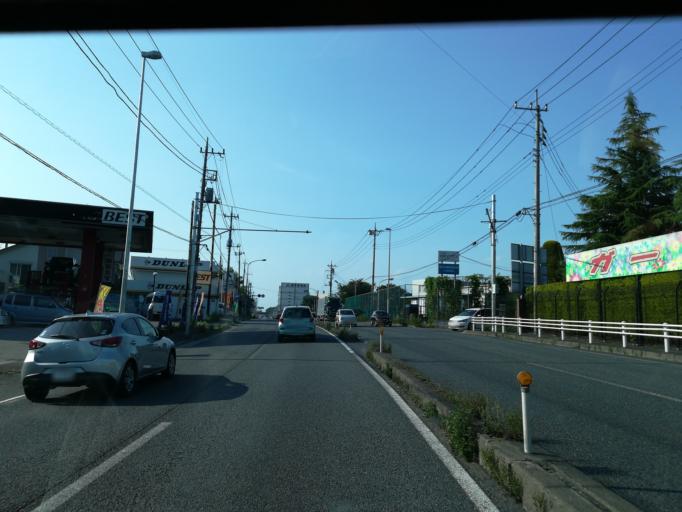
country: JP
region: Saitama
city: Sayama
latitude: 35.8073
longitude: 139.3790
